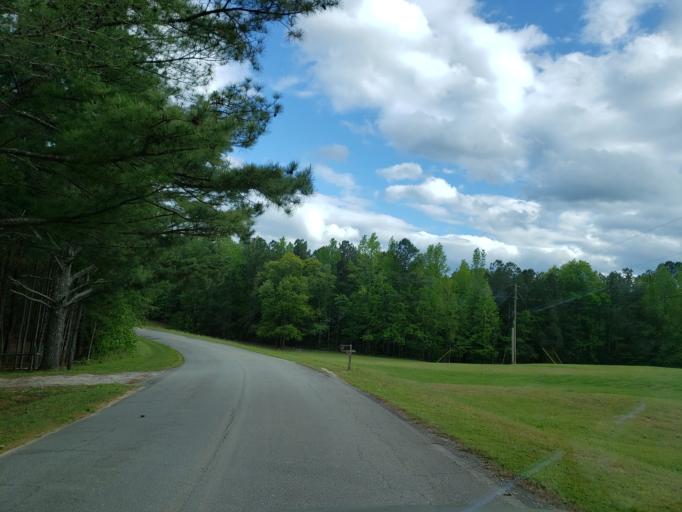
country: US
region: Georgia
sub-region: Haralson County
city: Tallapoosa
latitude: 33.8018
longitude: -85.3595
